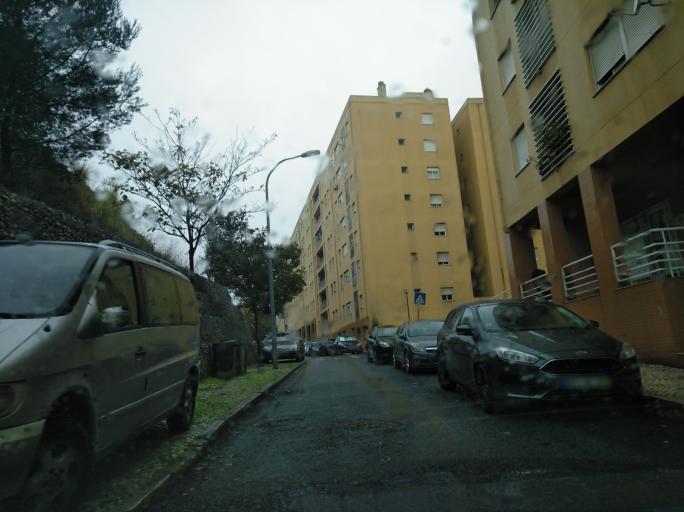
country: PT
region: Lisbon
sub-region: Lisbon
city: Lisbon
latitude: 38.7322
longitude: -9.1207
